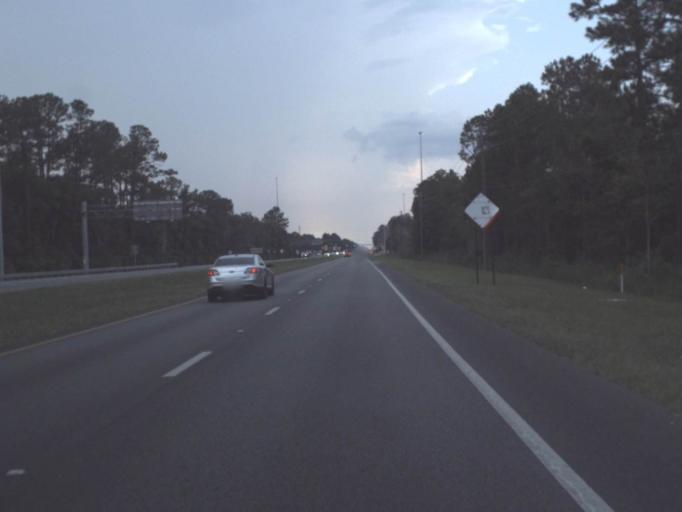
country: US
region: Florida
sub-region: Saint Johns County
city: Palm Valley
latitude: 30.1005
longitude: -81.4745
